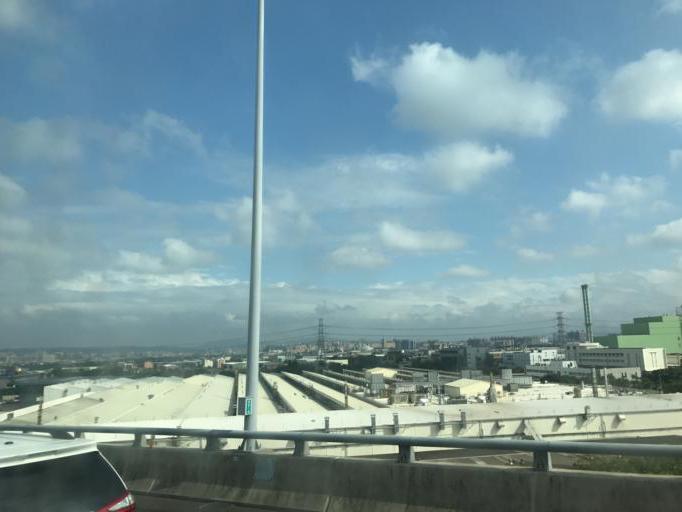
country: TW
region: Taiwan
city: Taoyuan City
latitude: 24.9954
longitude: 121.2447
